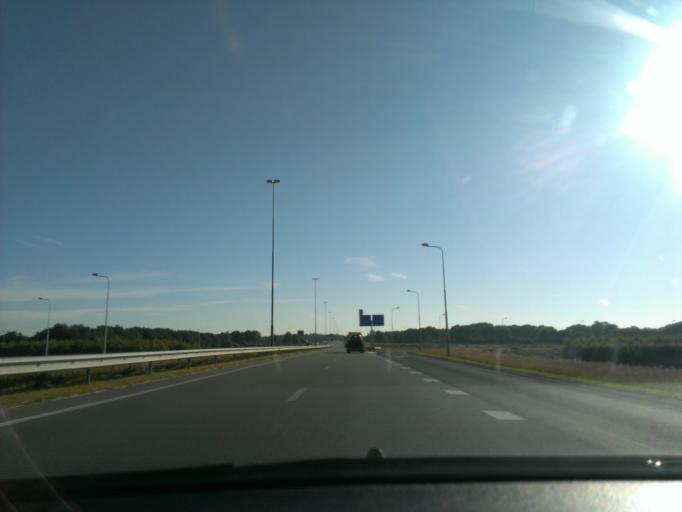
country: NL
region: Drenthe
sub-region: Gemeente Coevorden
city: Dalen
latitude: 52.7283
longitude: 6.7899
